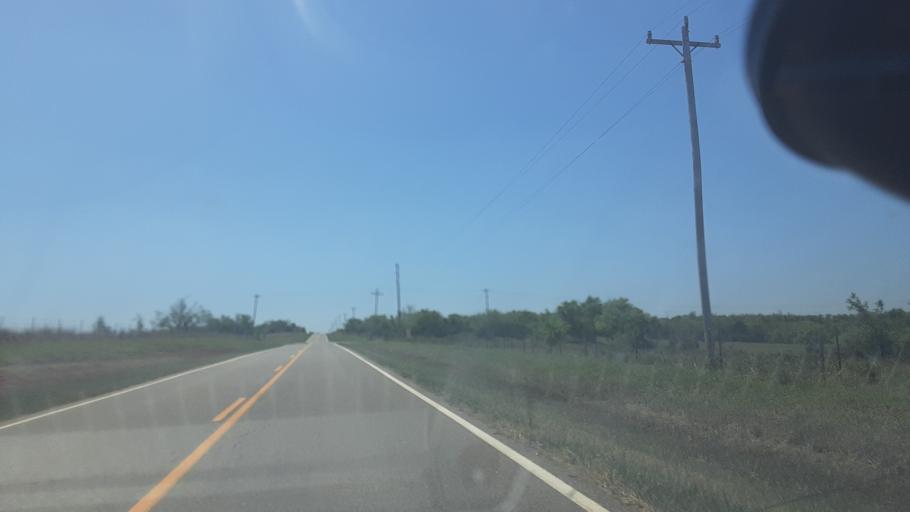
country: US
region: Oklahoma
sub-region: Logan County
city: Guthrie
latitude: 36.0301
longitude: -97.4078
